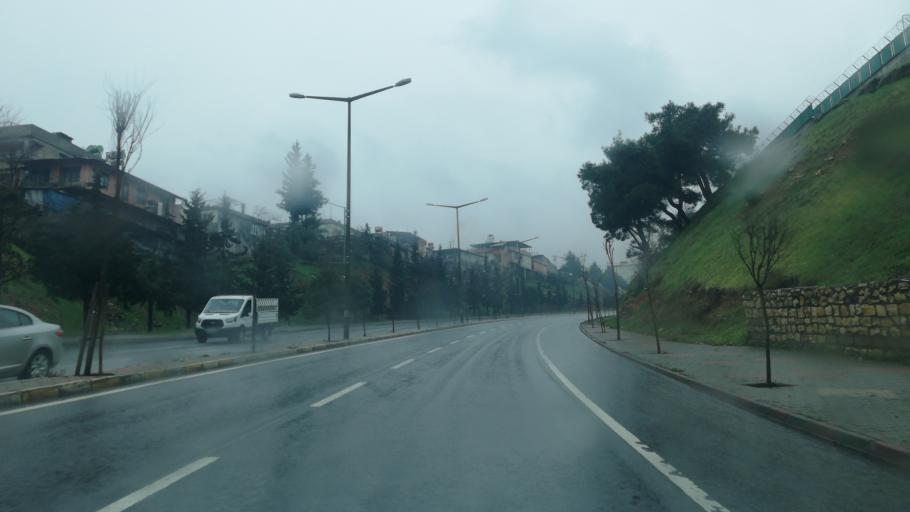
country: TR
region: Kahramanmaras
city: Kahramanmaras
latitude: 37.5942
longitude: 36.9255
